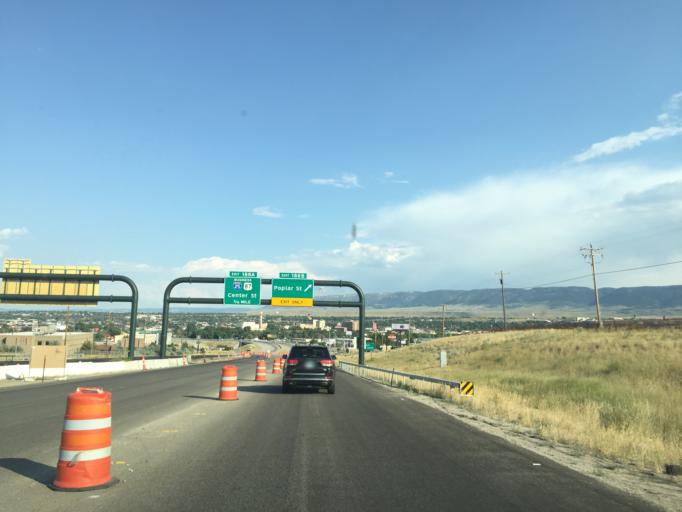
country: US
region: Wyoming
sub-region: Natrona County
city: Casper
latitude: 42.8615
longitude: -106.3397
